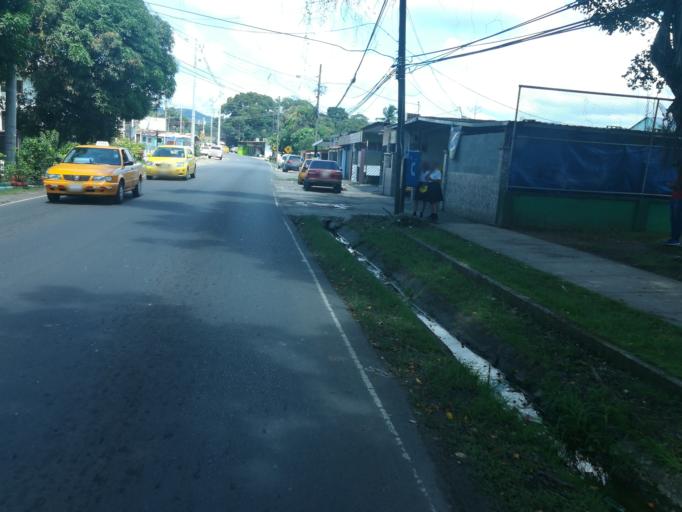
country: PA
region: Panama
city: Tocumen
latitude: 9.0810
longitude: -79.4042
